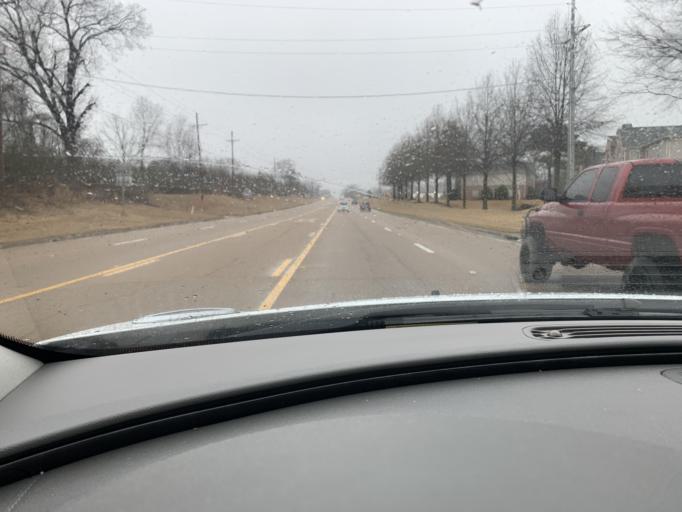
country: US
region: Mississippi
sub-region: De Soto County
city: Horn Lake
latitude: 34.9297
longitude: -90.0117
